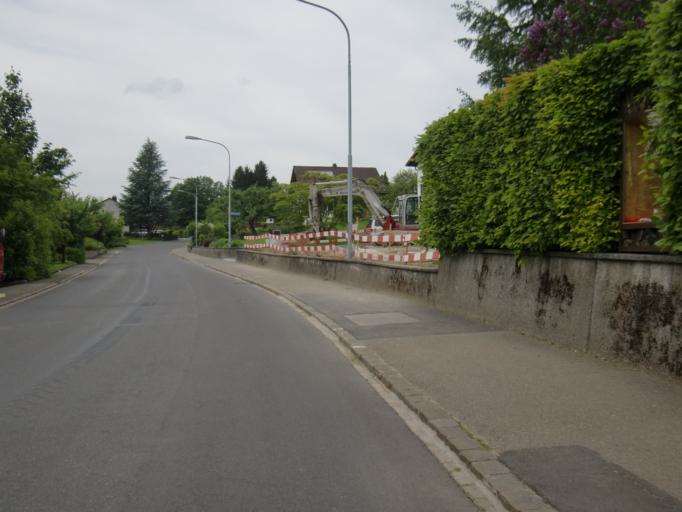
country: CH
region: Zurich
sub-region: Bezirk Hinwil
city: Tann
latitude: 47.2677
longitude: 8.8423
